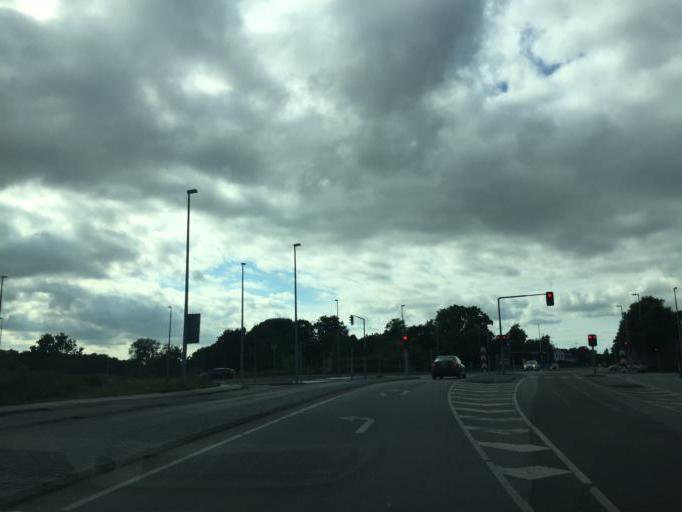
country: DK
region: South Denmark
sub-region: Odense Kommune
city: Odense
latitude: 55.4213
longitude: 10.3490
